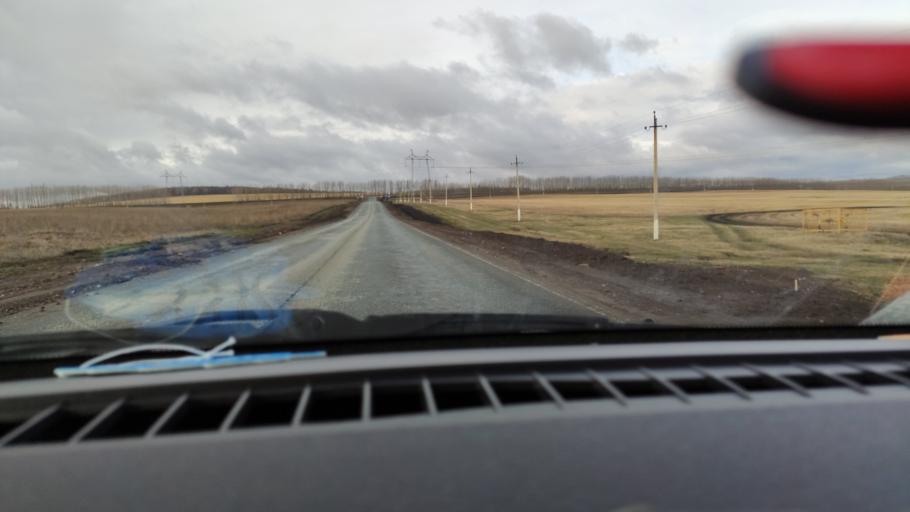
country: RU
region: Tatarstan
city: Russkiy Aktash
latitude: 55.0042
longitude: 51.7936
